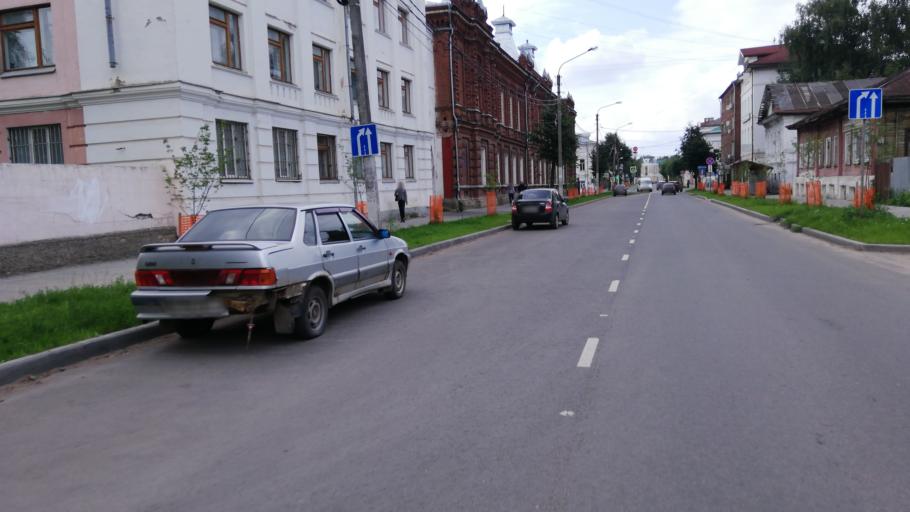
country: RU
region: Kostroma
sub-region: Kostromskoy Rayon
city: Kostroma
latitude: 57.7700
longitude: 40.9345
